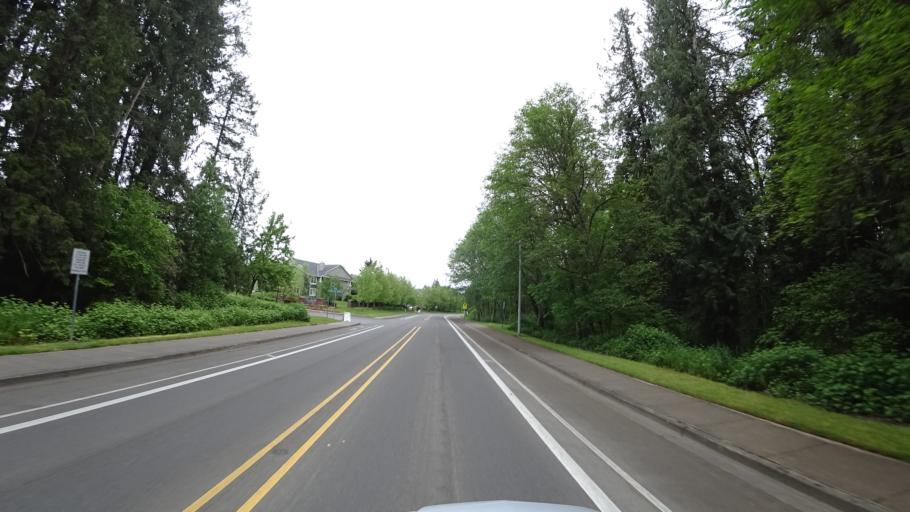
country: US
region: Oregon
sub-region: Washington County
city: Hillsboro
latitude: 45.5373
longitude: -122.9886
